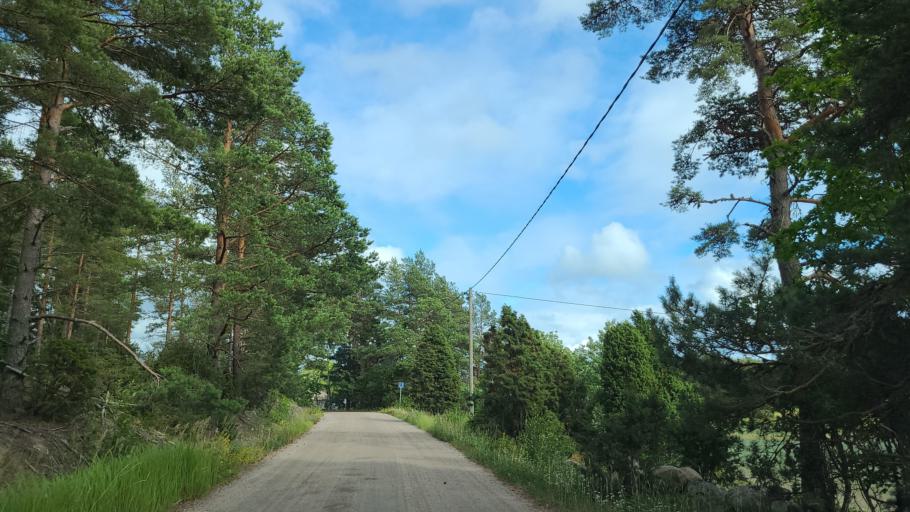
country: FI
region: Varsinais-Suomi
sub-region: Aboland-Turunmaa
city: Nagu
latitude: 60.1417
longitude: 21.7903
